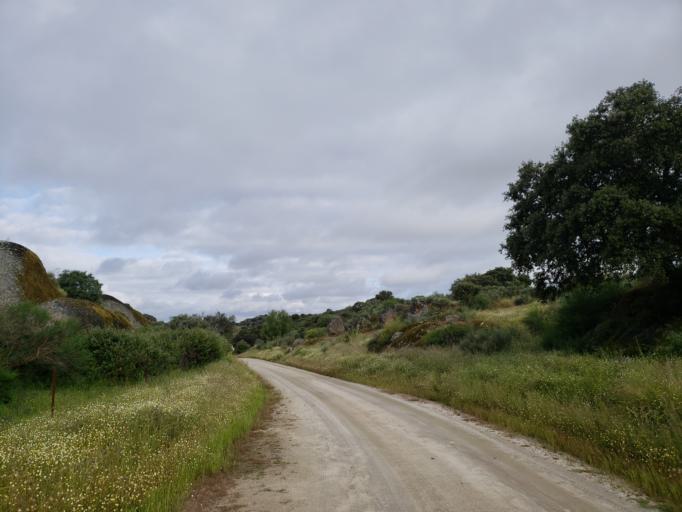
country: ES
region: Extremadura
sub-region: Provincia de Caceres
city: Malpartida de Caceres
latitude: 39.4253
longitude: -6.4880
